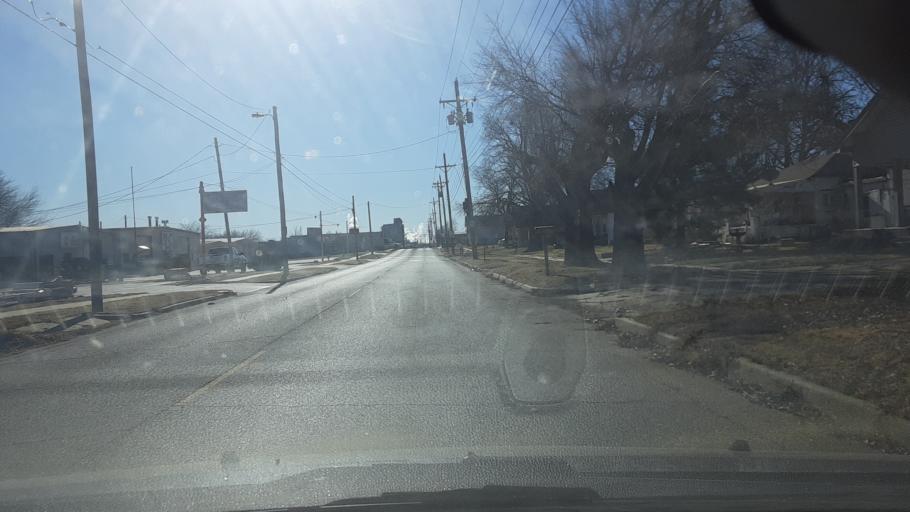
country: US
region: Oklahoma
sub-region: Kay County
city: Ponca City
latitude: 36.7114
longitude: -97.0853
